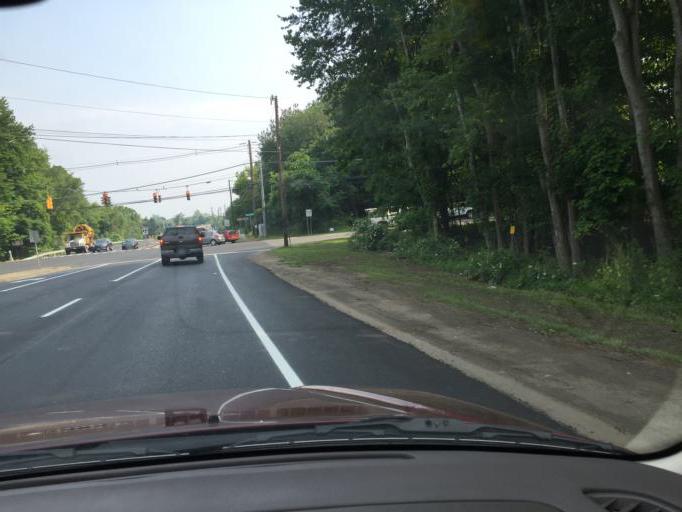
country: US
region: Connecticut
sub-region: Fairfield County
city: Westport
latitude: 41.1275
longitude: -73.3328
